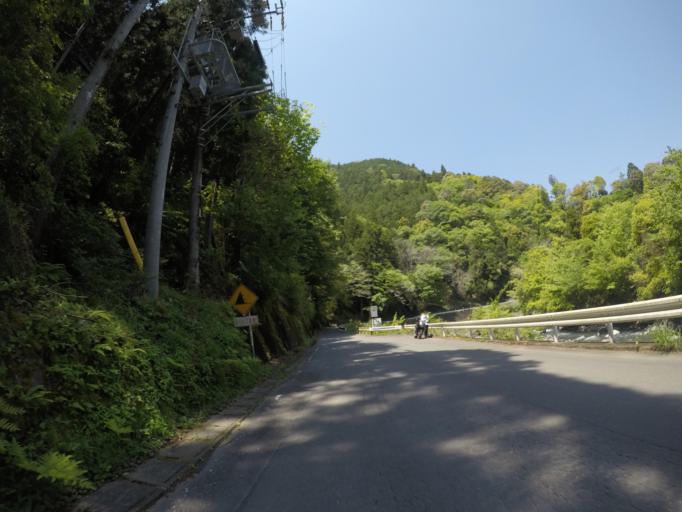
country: JP
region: Shizuoka
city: Shizuoka-shi
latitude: 35.1049
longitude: 138.2271
